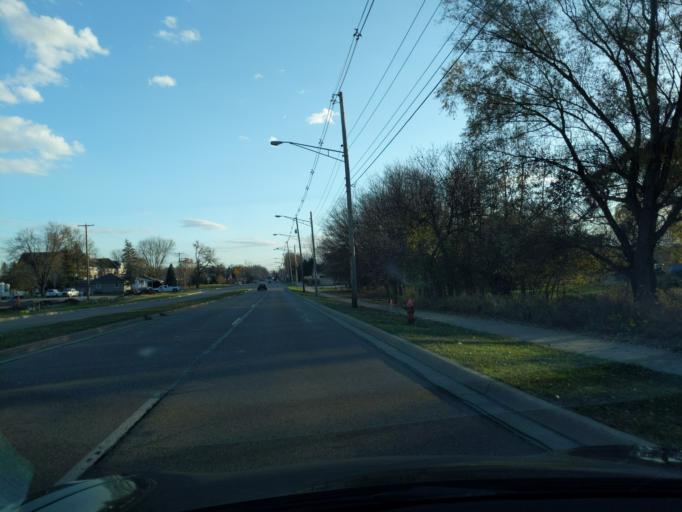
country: US
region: Michigan
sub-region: Ingham County
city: East Lansing
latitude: 42.7647
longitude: -84.4837
